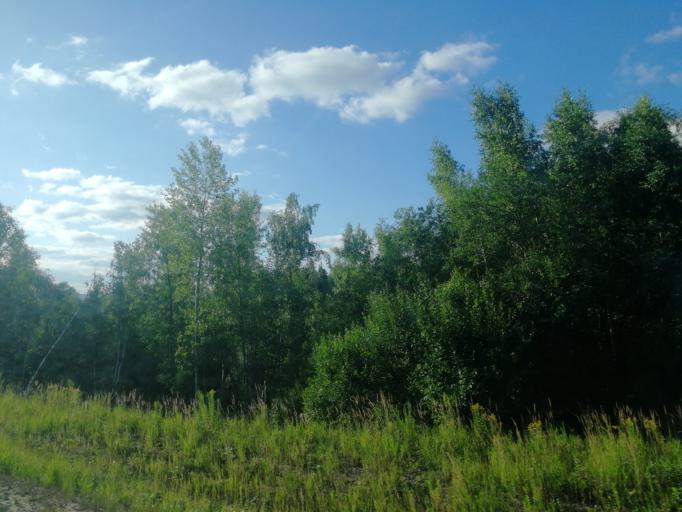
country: RU
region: Tula
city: Novogurovskiy
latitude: 54.2798
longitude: 37.2144
